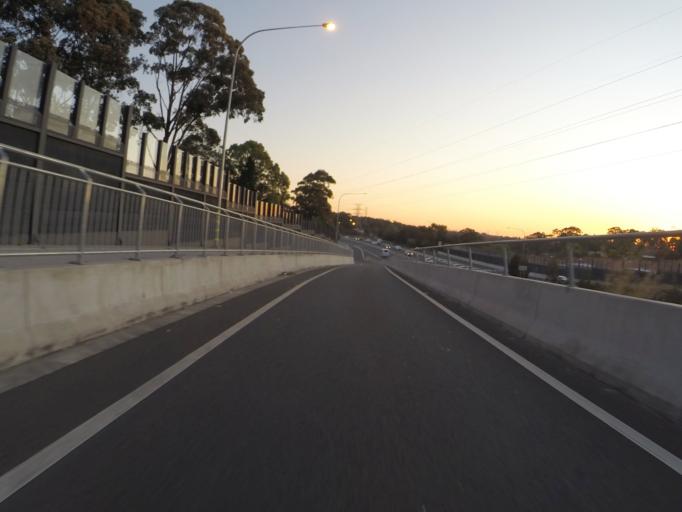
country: AU
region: New South Wales
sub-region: Bankstown
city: Padstow
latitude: -33.9668
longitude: 151.0333
